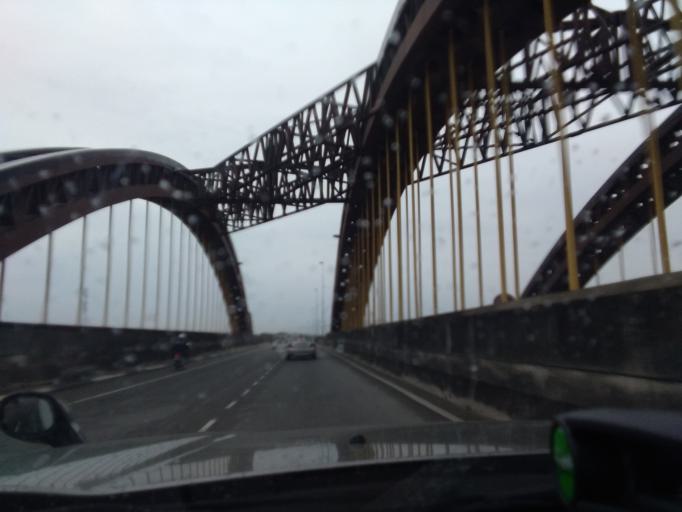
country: MY
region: Penang
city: Nibong Tebal
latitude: 5.1716
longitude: 100.4794
